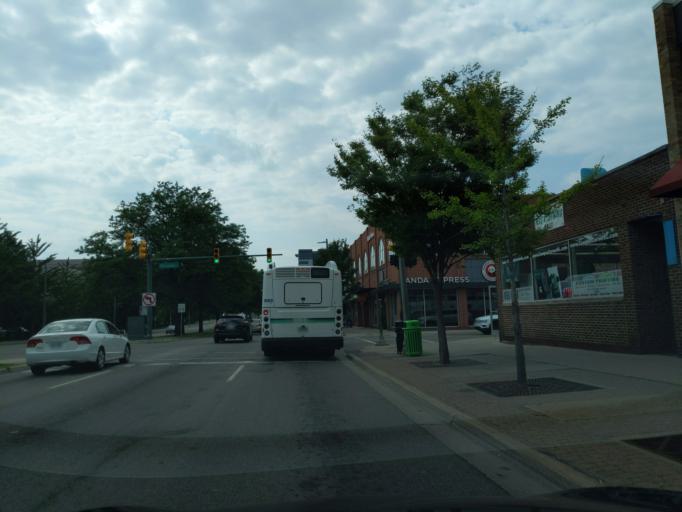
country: US
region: Michigan
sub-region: Ingham County
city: East Lansing
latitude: 42.7338
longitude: -84.4782
